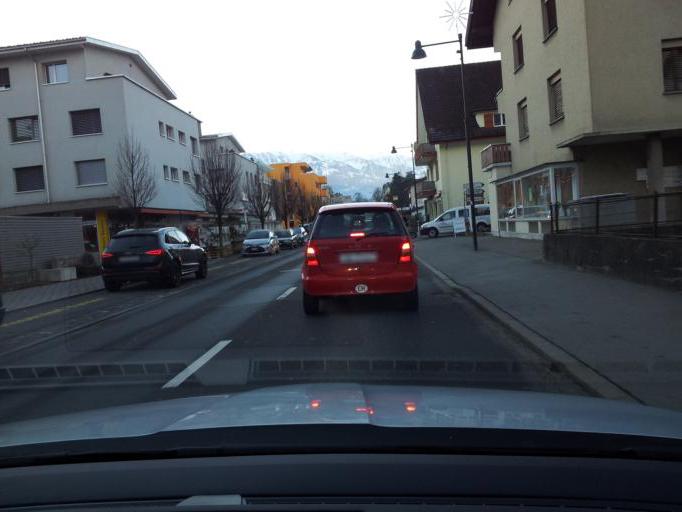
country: CH
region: Obwalden
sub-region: Obwalden
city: Alpnach
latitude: 46.9406
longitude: 8.2709
